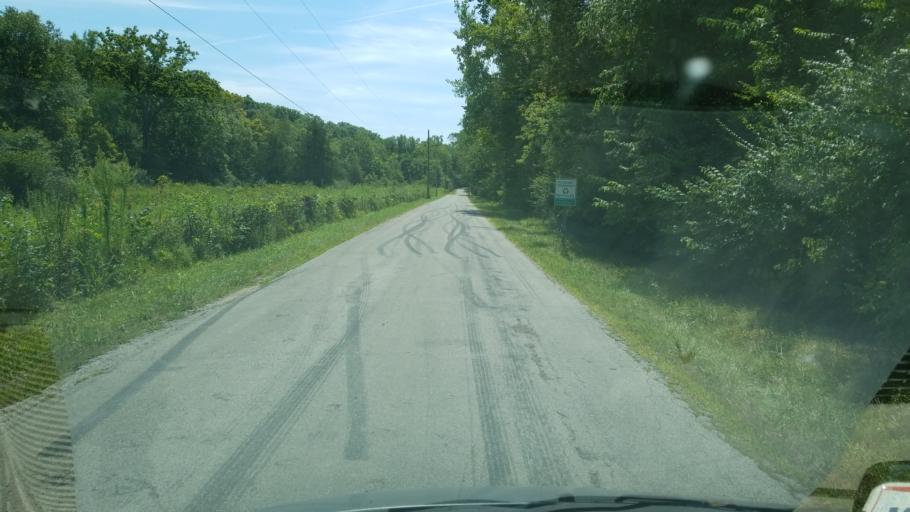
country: US
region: Ohio
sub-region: Franklin County
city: Lake Darby
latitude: 39.8499
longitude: -83.2112
